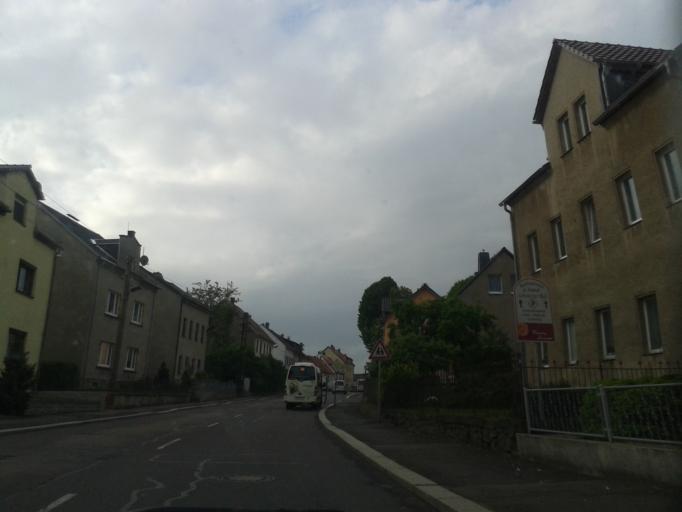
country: DE
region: Saxony
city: Nossen
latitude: 51.0324
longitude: 13.3050
